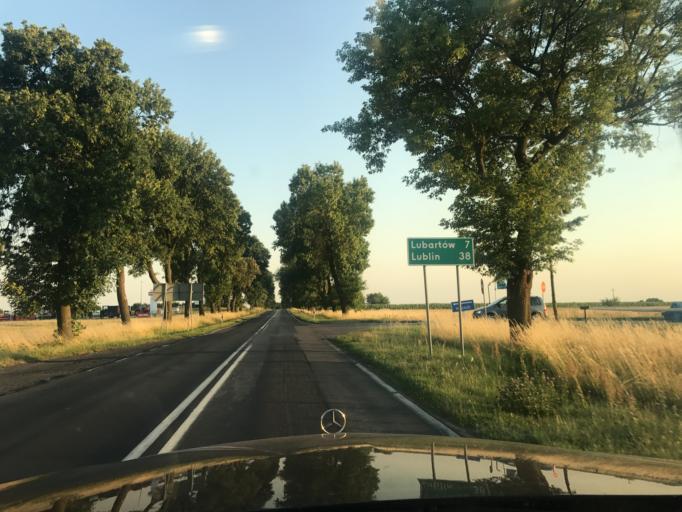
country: PL
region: Lublin Voivodeship
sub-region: Powiat lubartowski
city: Niedzwiada
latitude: 51.5109
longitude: 22.6652
